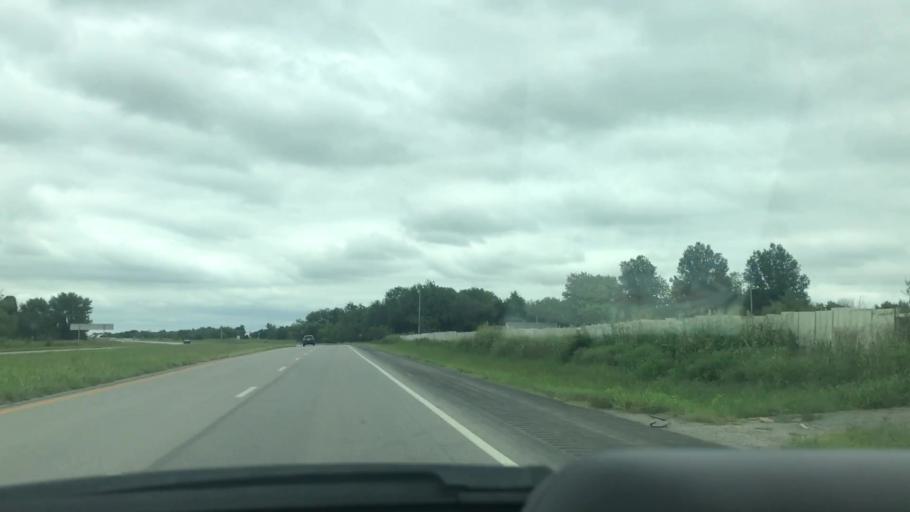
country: US
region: Oklahoma
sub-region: Mayes County
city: Pryor
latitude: 36.3817
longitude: -95.2934
